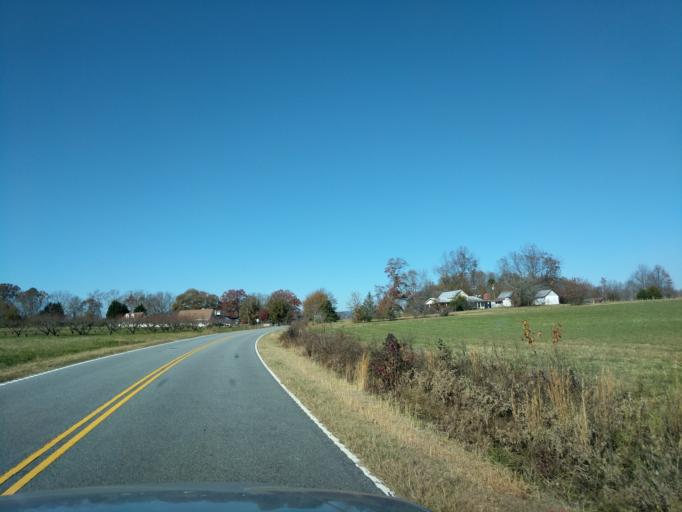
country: US
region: South Carolina
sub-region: Spartanburg County
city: Landrum
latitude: 35.0849
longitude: -82.2159
